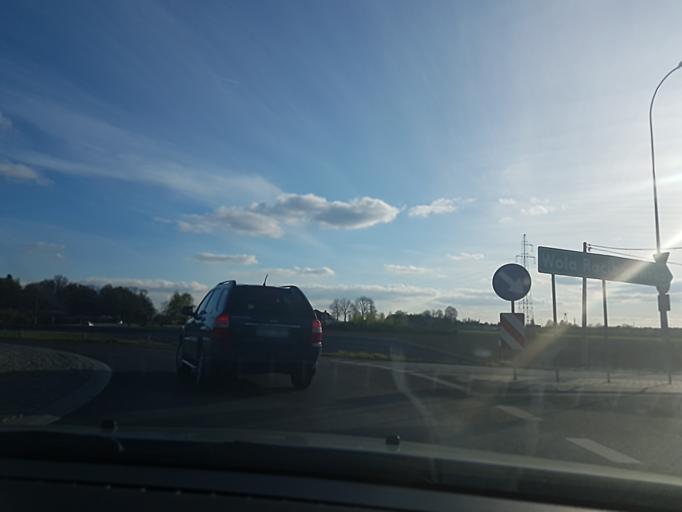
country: PL
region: Lodz Voivodeship
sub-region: Powiat kutnowski
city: Strzelce
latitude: 52.2829
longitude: 19.3952
